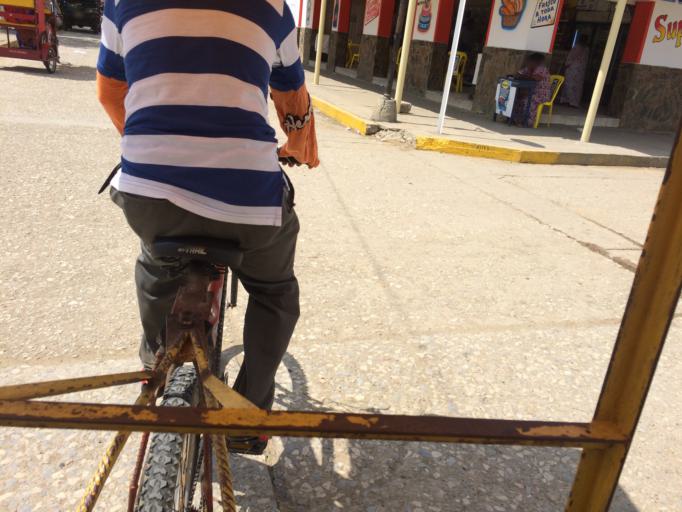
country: CO
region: La Guajira
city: Manaure
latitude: 11.7761
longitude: -72.4463
